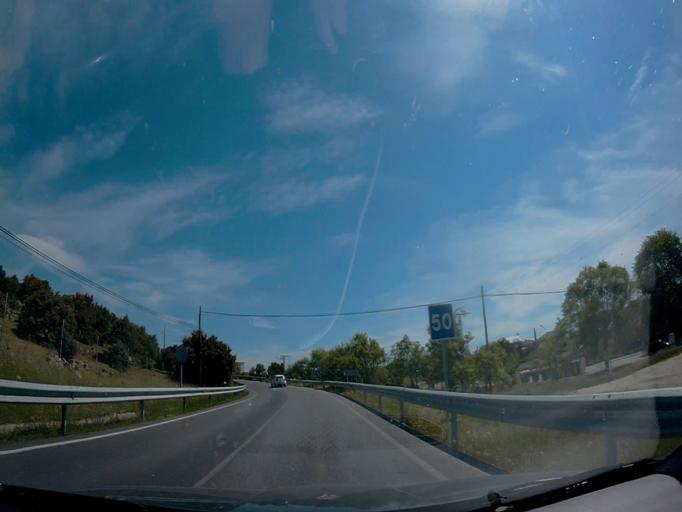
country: ES
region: Madrid
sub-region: Provincia de Madrid
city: Hoyo de Manzanares
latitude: 40.6060
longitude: -3.9045
